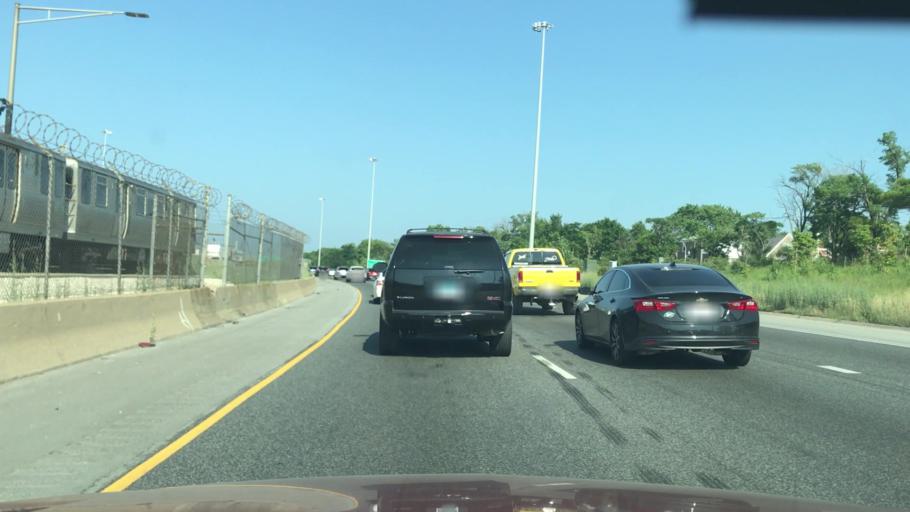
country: US
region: Illinois
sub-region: Cook County
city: Calumet Park
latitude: 41.7133
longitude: -87.6194
